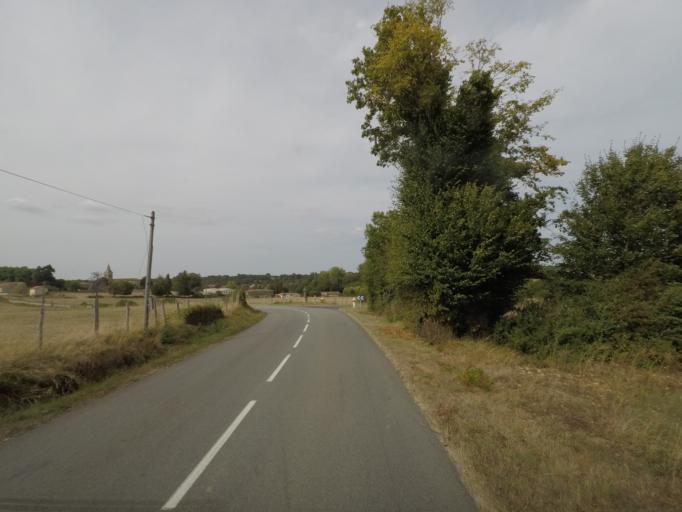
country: FR
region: Poitou-Charentes
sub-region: Departement de la Charente
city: Champagne-Mouton
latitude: 45.9873
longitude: 0.4135
